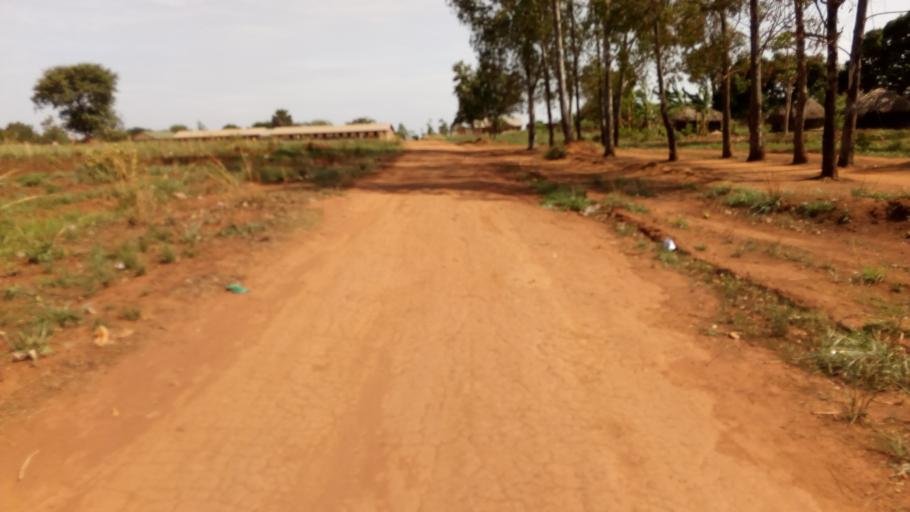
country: UG
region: Northern Region
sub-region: Gulu District
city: Gulu
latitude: 2.7883
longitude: 32.3211
